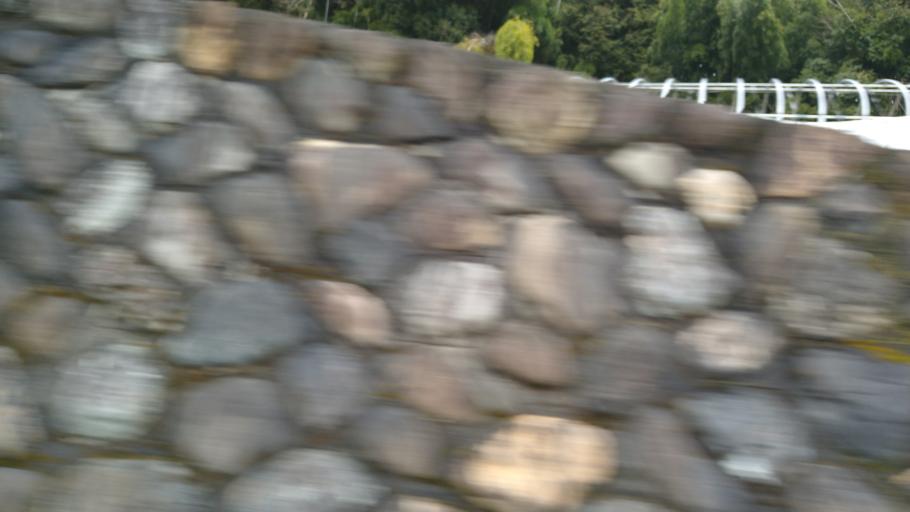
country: JP
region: Kyoto
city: Maizuru
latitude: 35.3850
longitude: 135.3580
